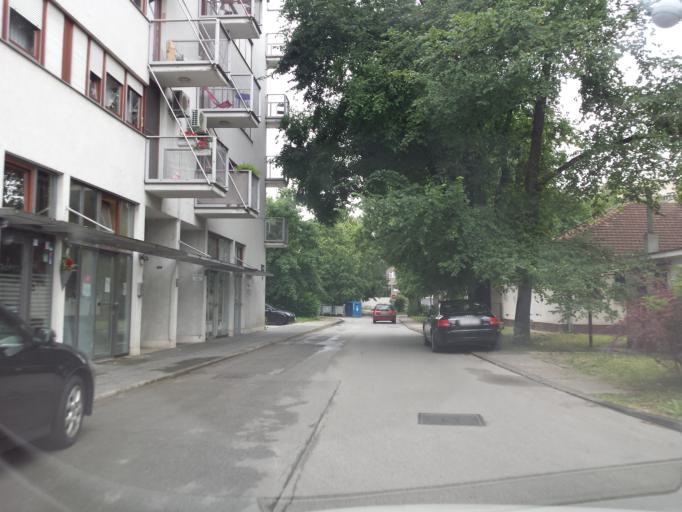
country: HR
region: Grad Zagreb
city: Zagreb - Centar
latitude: 45.7952
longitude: 15.9616
